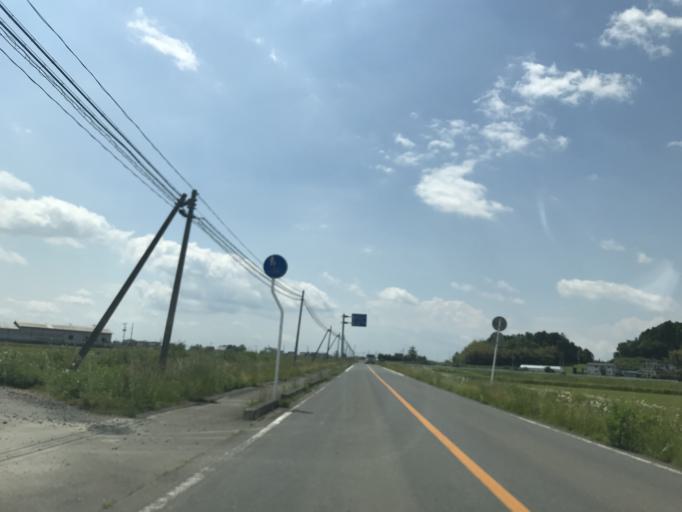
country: JP
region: Miyagi
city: Kogota
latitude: 38.6127
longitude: 141.0208
